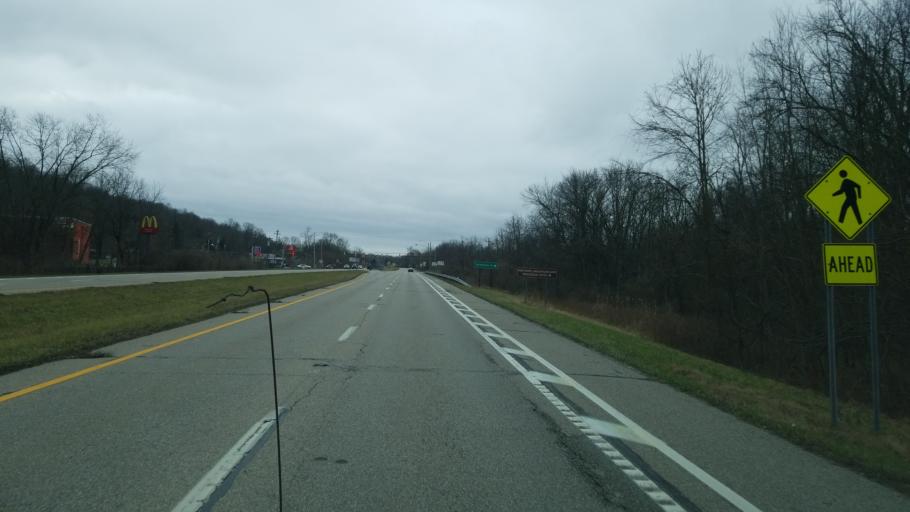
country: US
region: Ohio
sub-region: Clermont County
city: New Richmond
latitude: 38.9580
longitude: -84.2824
